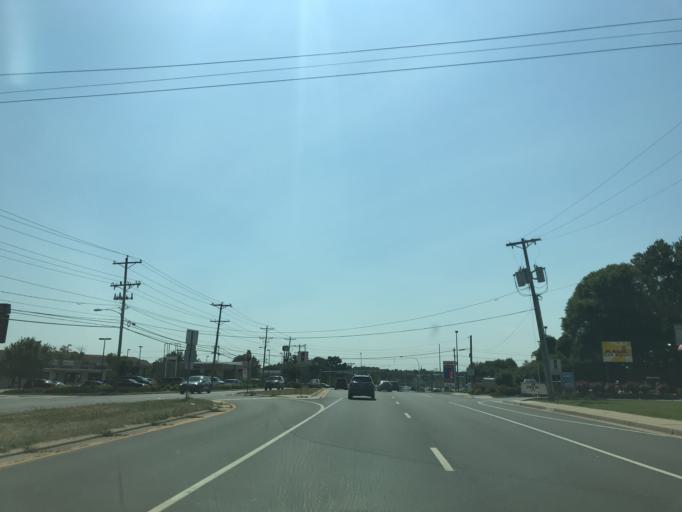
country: US
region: Delaware
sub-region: New Castle County
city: Bellefonte
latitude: 39.8290
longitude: -75.5418
